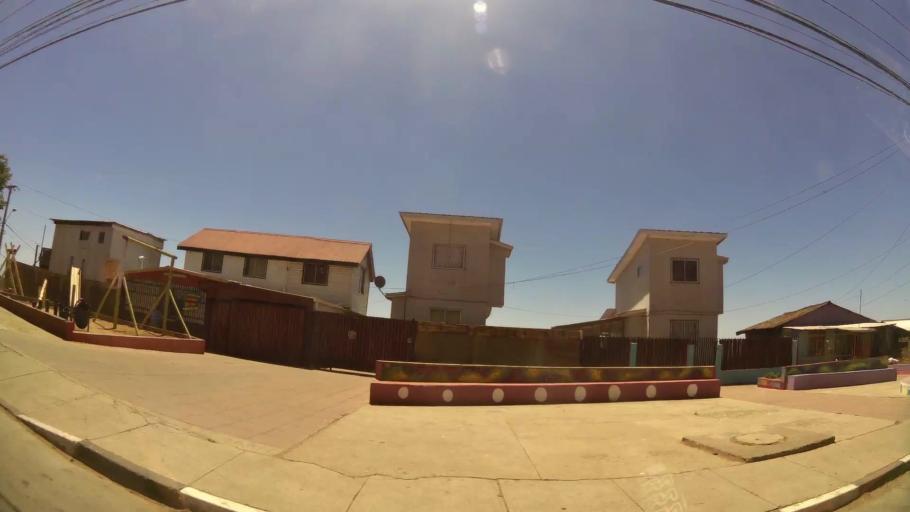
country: CL
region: Valparaiso
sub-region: Provincia de Valparaiso
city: Valparaiso
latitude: -33.0589
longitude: -71.6401
